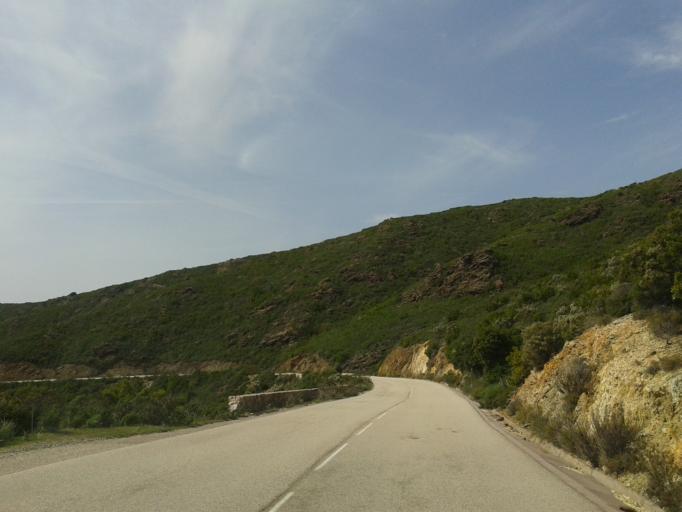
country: FR
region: Corsica
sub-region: Departement de la Haute-Corse
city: Saint-Florent
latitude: 42.6610
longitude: 9.1316
